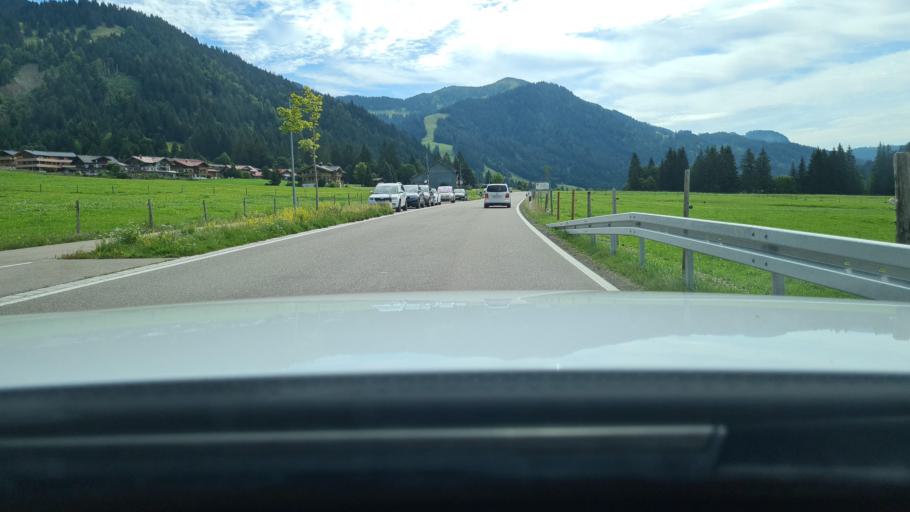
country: DE
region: Bavaria
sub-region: Swabia
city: Balderschwang
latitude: 47.4651
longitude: 10.1110
